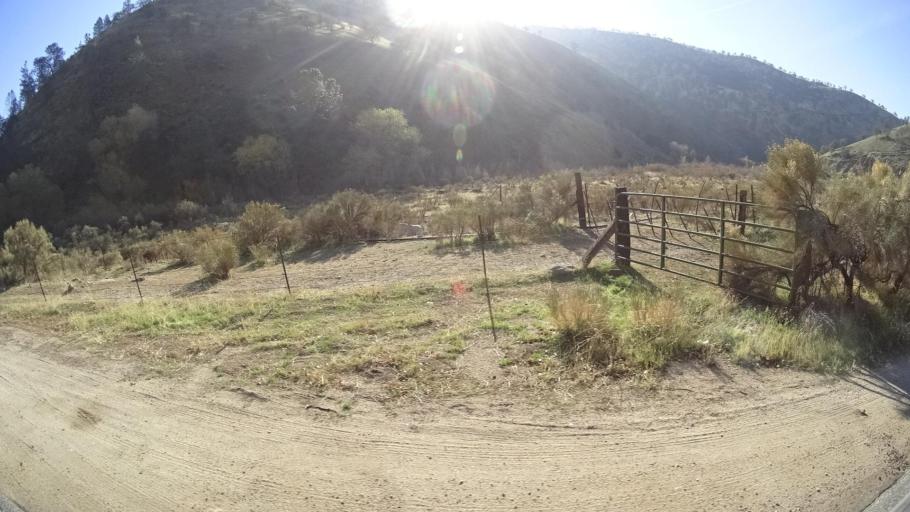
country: US
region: California
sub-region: Kern County
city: Bear Valley Springs
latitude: 35.3077
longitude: -118.5834
